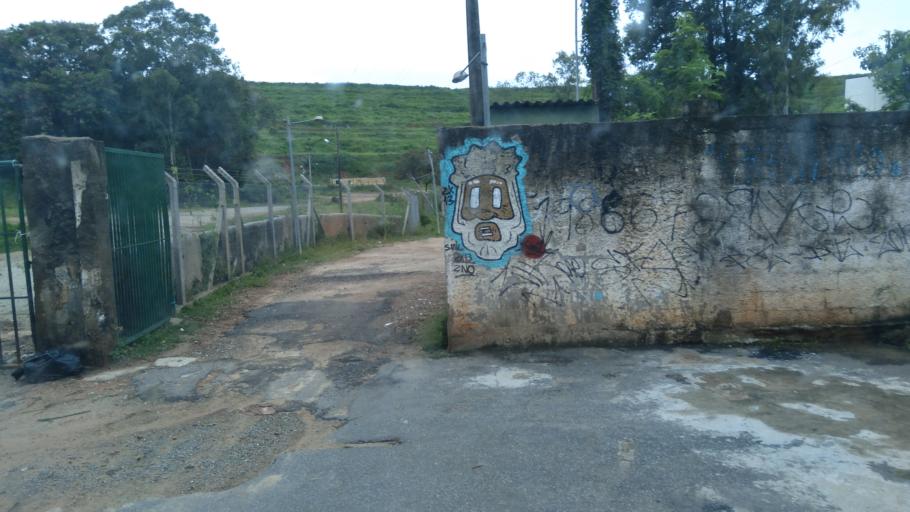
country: BR
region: Minas Gerais
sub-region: Contagem
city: Contagem
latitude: -19.9099
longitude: -44.0152
